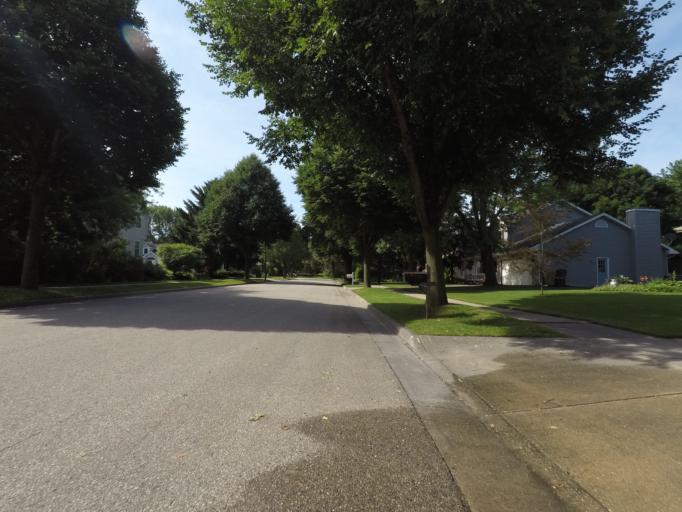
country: US
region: Wisconsin
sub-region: Dane County
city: Middleton
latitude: 43.0774
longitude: -89.4938
